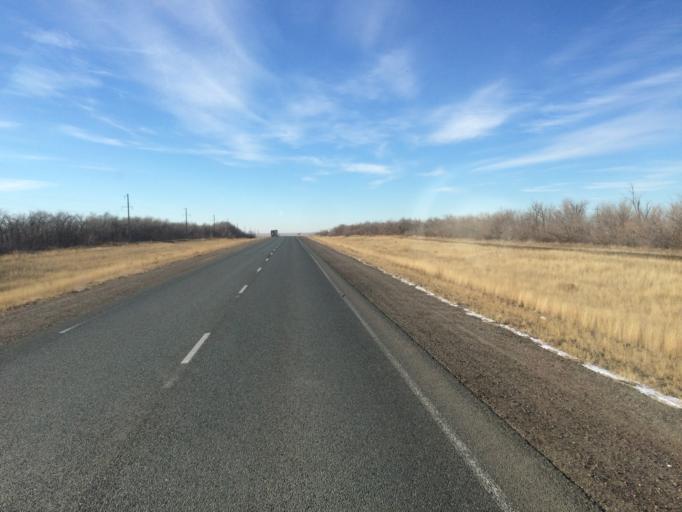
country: KZ
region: Aqtoebe
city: Aqtobe
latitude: 50.2474
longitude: 56.7982
